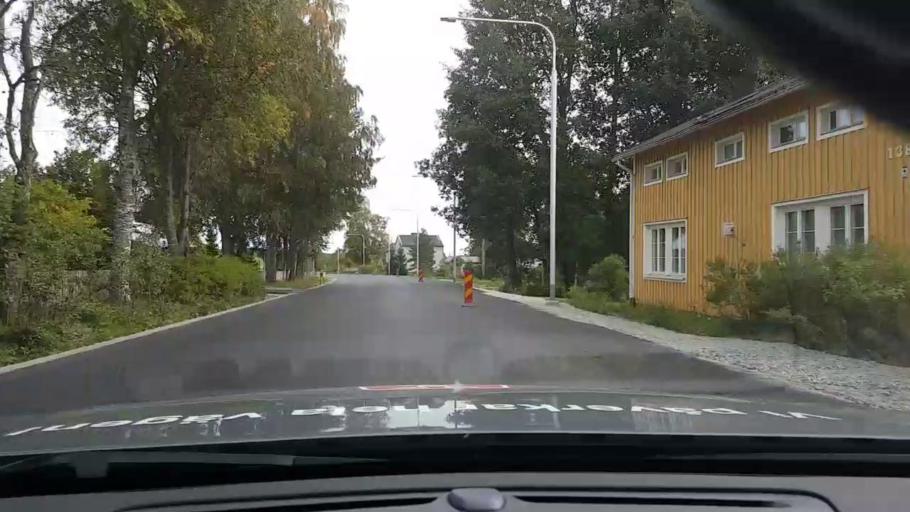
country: SE
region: Vaesternorrland
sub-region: OErnskoeldsviks Kommun
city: Bjasta
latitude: 63.2889
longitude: 18.4487
